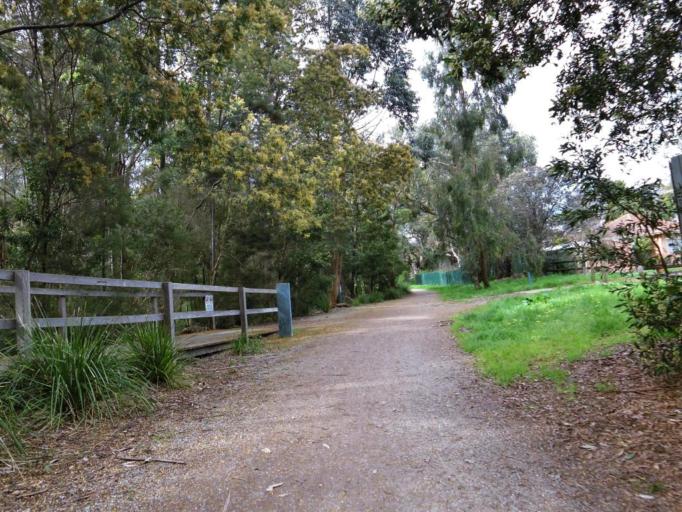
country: AU
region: Victoria
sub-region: Maroondah
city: Ringwood East
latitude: -37.8063
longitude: 145.2382
